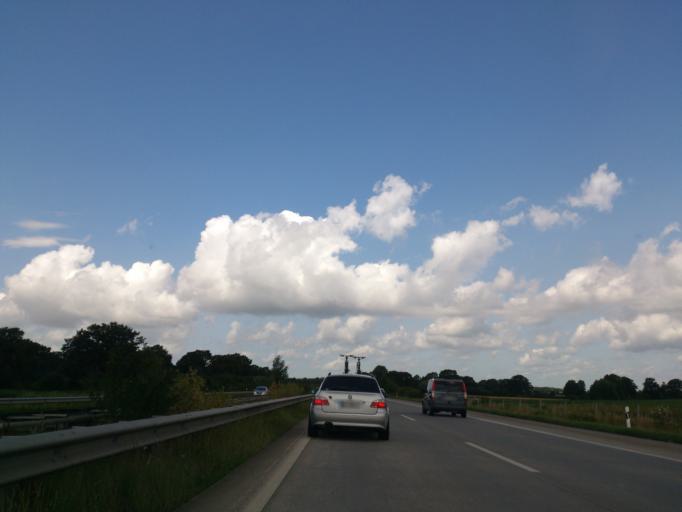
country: DE
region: Schleswig-Holstein
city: Dageling
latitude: 53.8814
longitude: 9.5478
